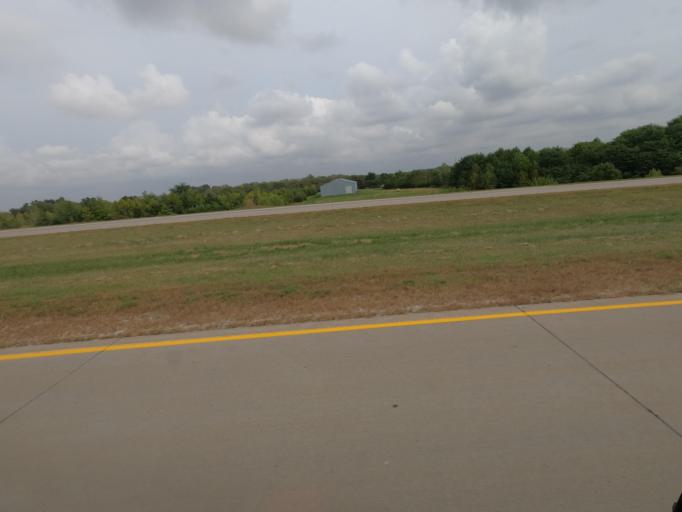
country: US
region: Iowa
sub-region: Wapello County
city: Ottumwa
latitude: 41.0737
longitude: -92.3940
